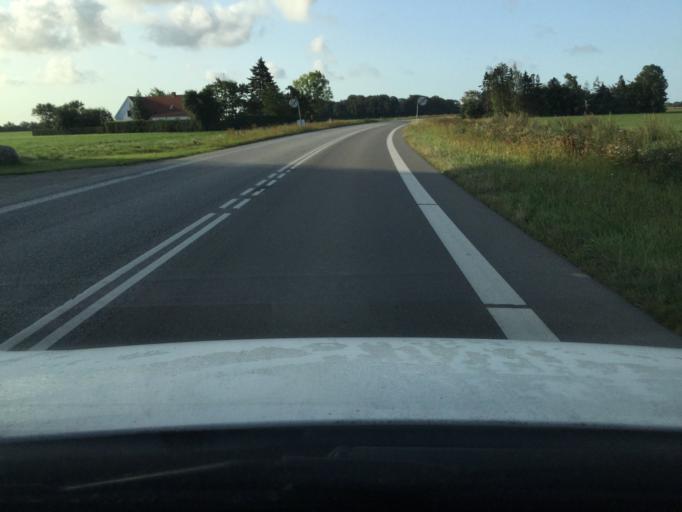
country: DK
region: Zealand
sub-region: Lolland Kommune
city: Rodby
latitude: 54.7768
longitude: 11.2995
